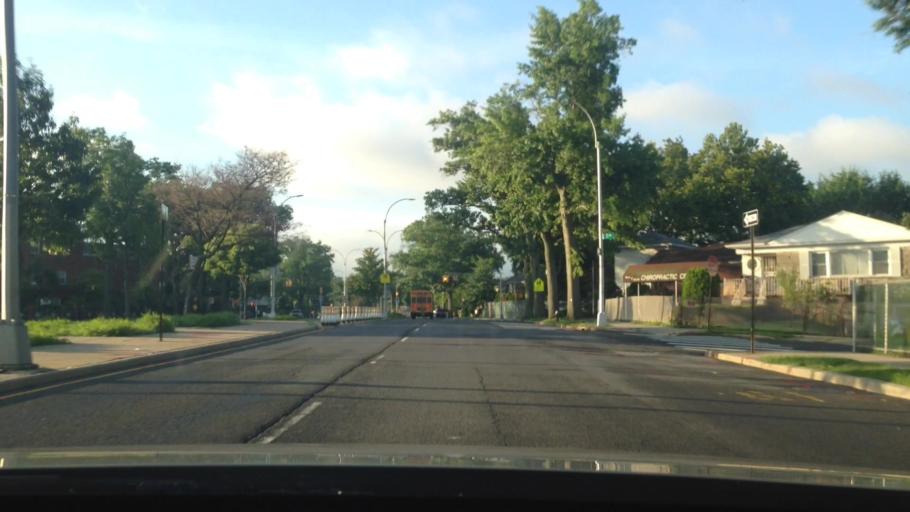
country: US
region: New York
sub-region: Nassau County
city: East Atlantic Beach
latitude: 40.7792
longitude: -73.8020
